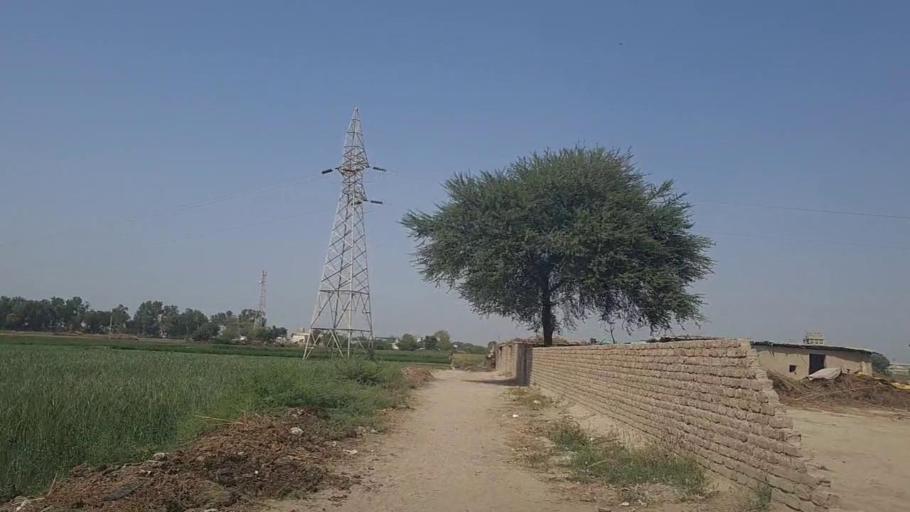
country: PK
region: Sindh
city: Naukot
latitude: 24.8423
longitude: 69.4175
